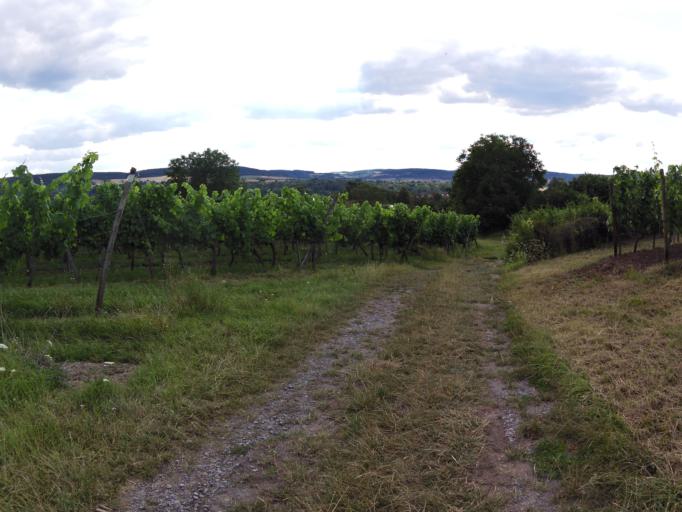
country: DE
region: Bavaria
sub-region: Regierungsbezirk Unterfranken
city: Thungersheim
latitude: 49.8842
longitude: 9.8519
